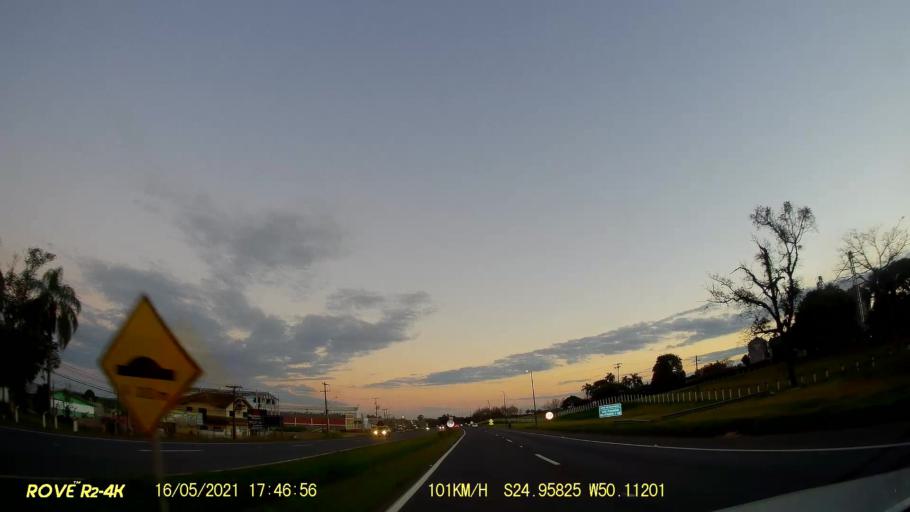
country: BR
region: Parana
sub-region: Carambei
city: Carambei
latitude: -24.9584
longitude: -50.1120
